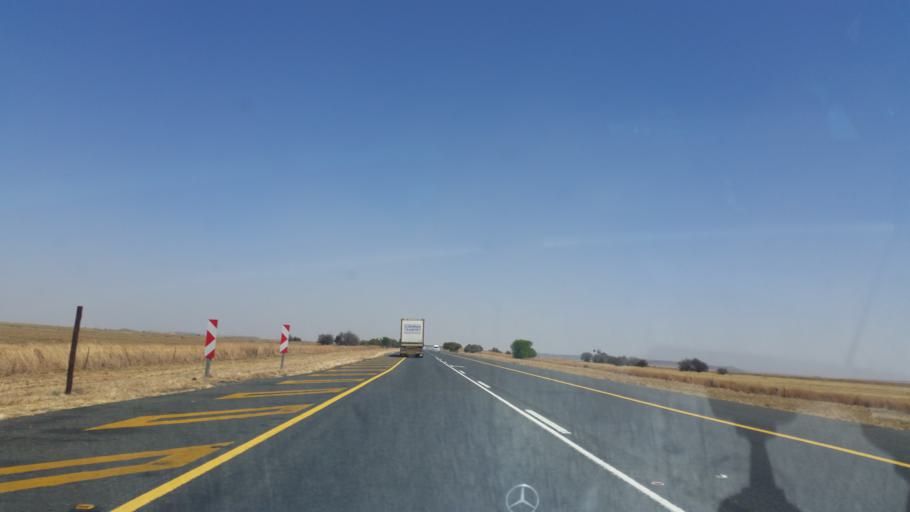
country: ZA
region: Orange Free State
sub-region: Lejweleputswa District Municipality
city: Winburg
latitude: -28.6485
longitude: 26.8786
